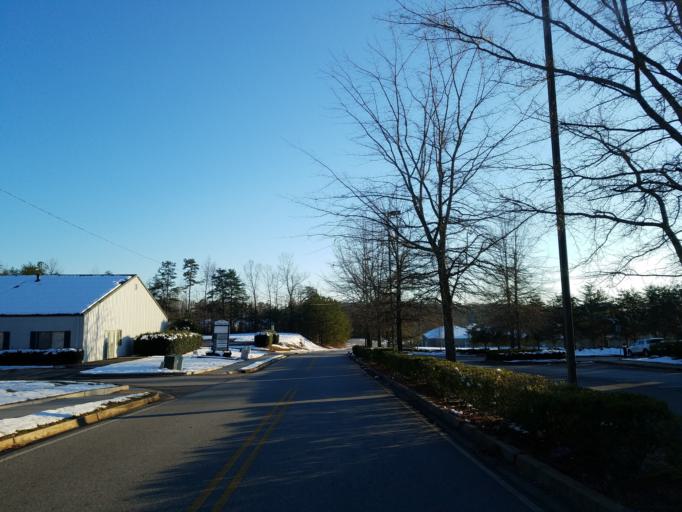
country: US
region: Georgia
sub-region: Dawson County
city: Dawsonville
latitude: 34.4189
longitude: -84.1079
